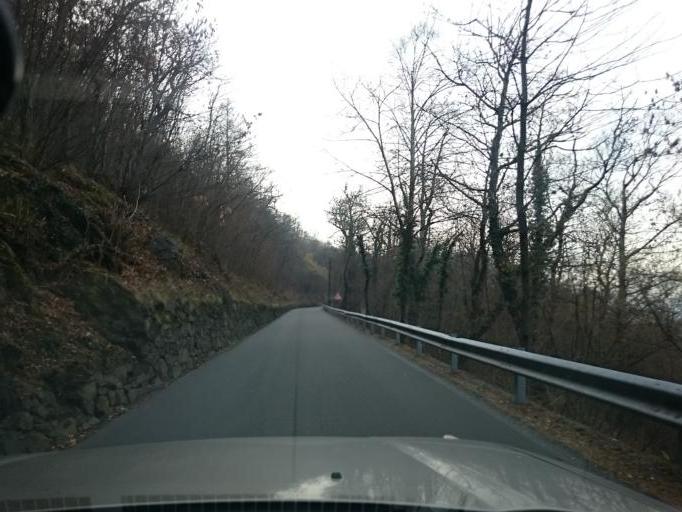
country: IT
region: Lombardy
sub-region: Provincia di Sondrio
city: Villa
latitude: 46.1824
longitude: 10.1332
